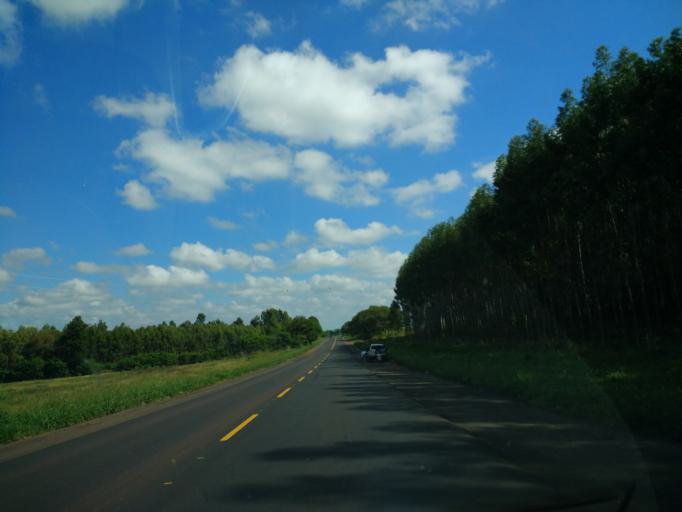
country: BR
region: Parana
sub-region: Umuarama
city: Umuarama
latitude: -23.8653
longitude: -53.3893
